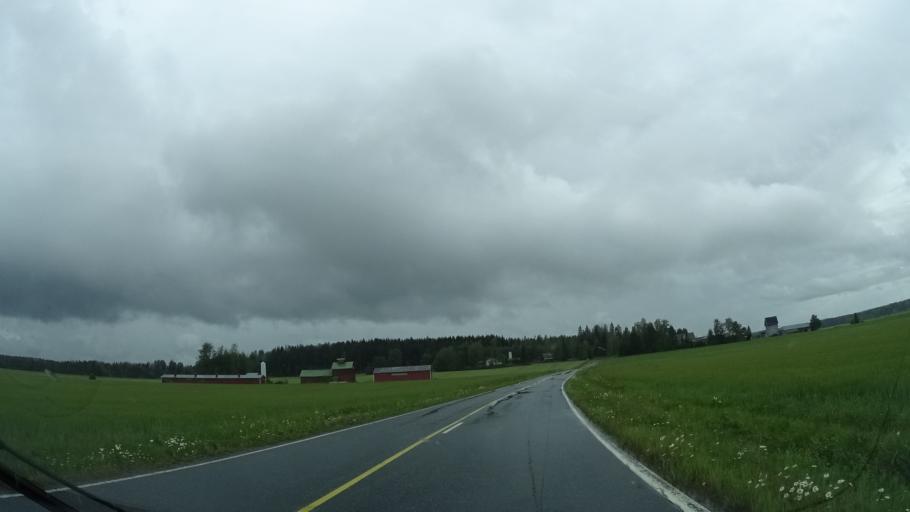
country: FI
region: Haeme
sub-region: Forssa
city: Humppila
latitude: 61.0013
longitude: 23.2516
